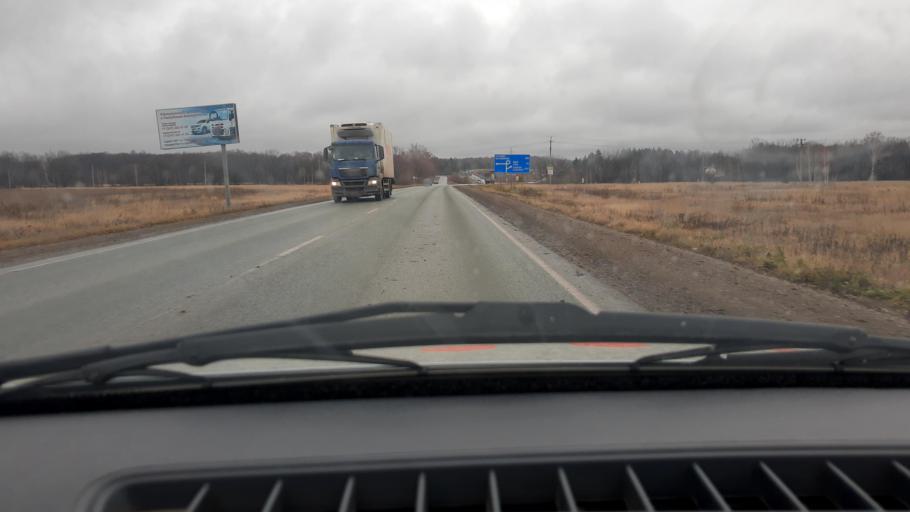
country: RU
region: Bashkortostan
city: Iglino
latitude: 54.7484
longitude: 56.2949
